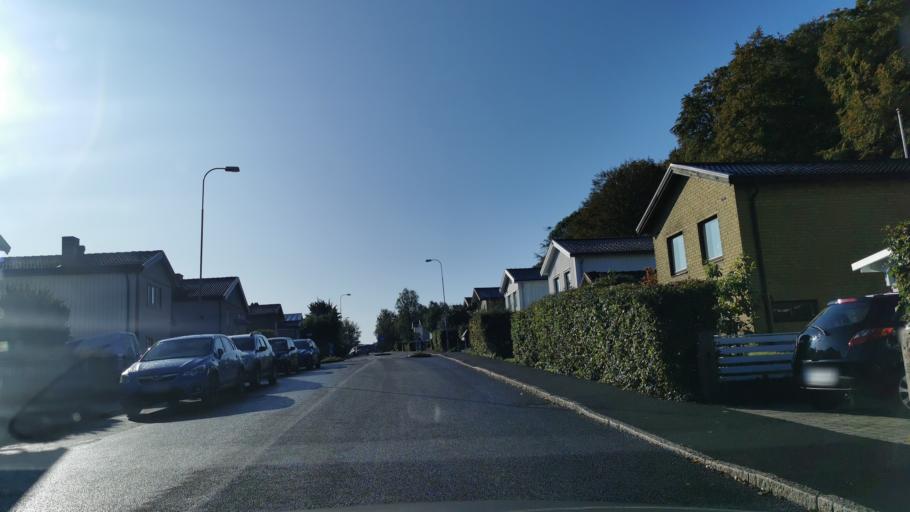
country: SE
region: Vaestra Goetaland
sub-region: Goteborg
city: Eriksbo
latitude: 57.7265
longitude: 12.0518
